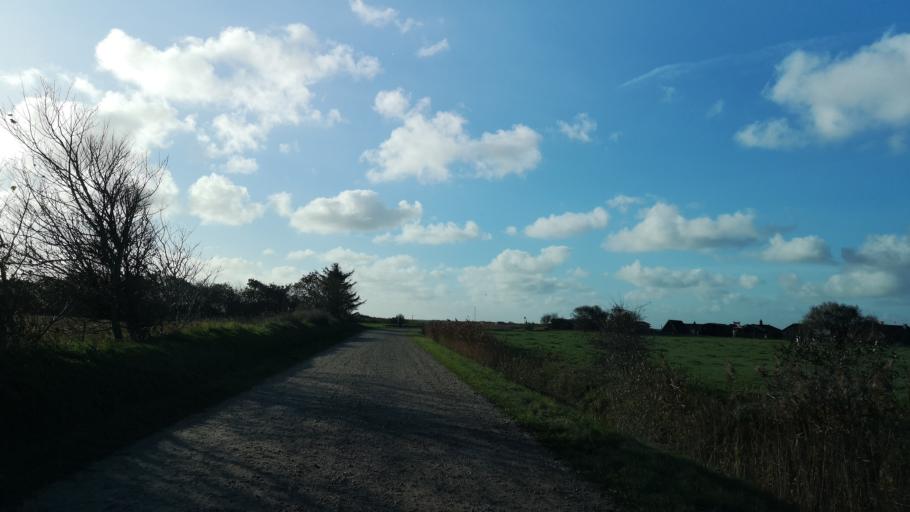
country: DK
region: Central Jutland
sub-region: Ringkobing-Skjern Kommune
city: Skjern
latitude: 55.8685
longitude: 8.3309
